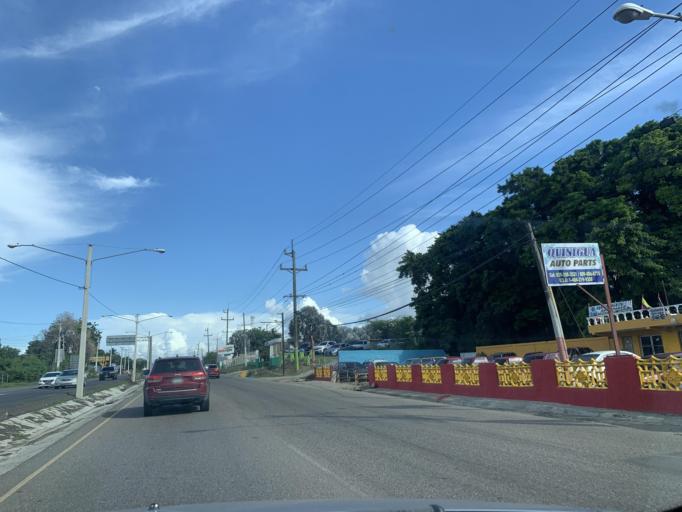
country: DO
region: Santiago
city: Palmar Arriba
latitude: 19.5158
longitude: -70.7621
